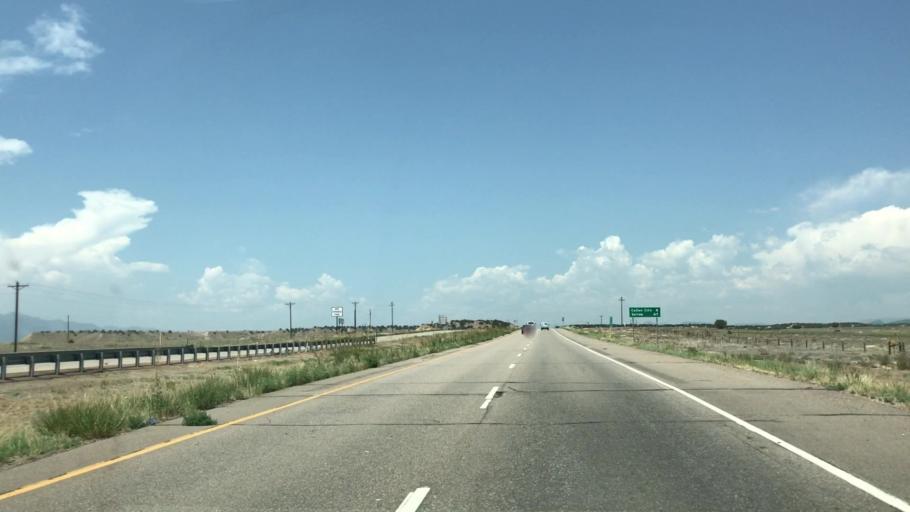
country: US
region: Colorado
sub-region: Fremont County
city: Penrose
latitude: 38.4208
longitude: -105.0536
